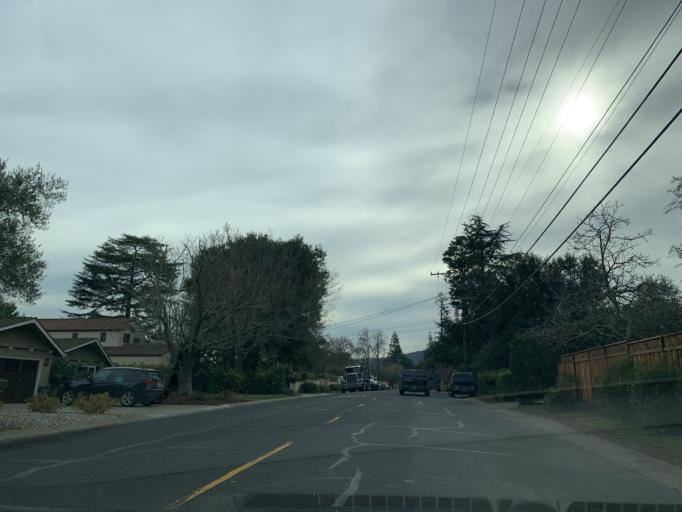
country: US
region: California
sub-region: Santa Clara County
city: Los Altos
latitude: 37.3706
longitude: -122.1020
